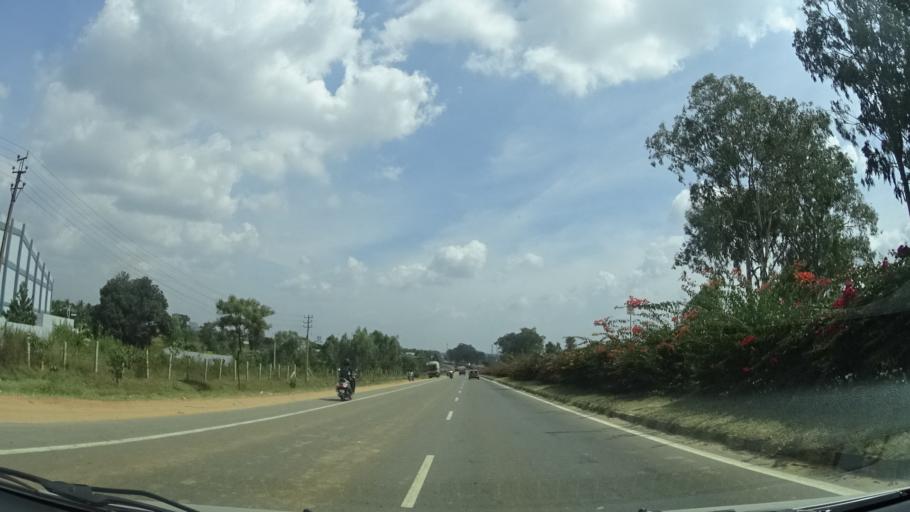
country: IN
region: Karnataka
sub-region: Bangalore Rural
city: Nelamangala
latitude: 13.1568
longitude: 77.3277
